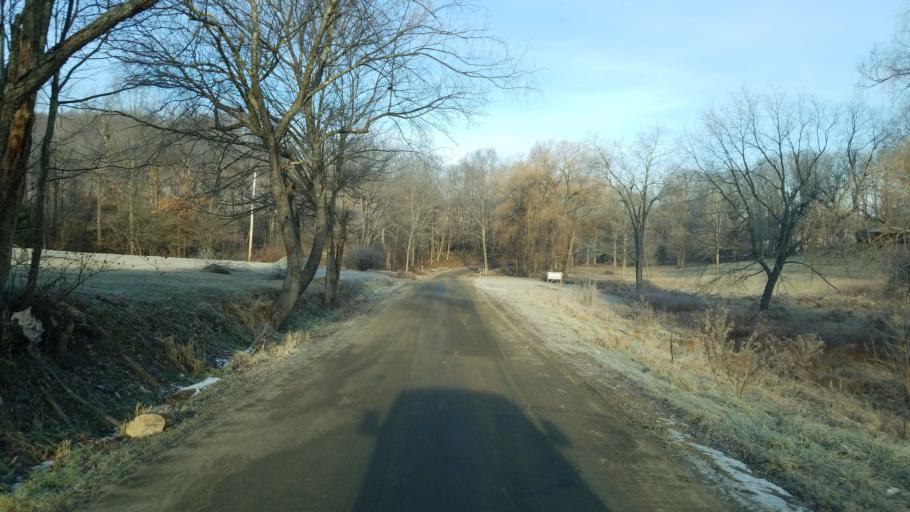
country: US
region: Pennsylvania
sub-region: Indiana County
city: Chevy Chase Heights
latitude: 40.8590
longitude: -79.2620
